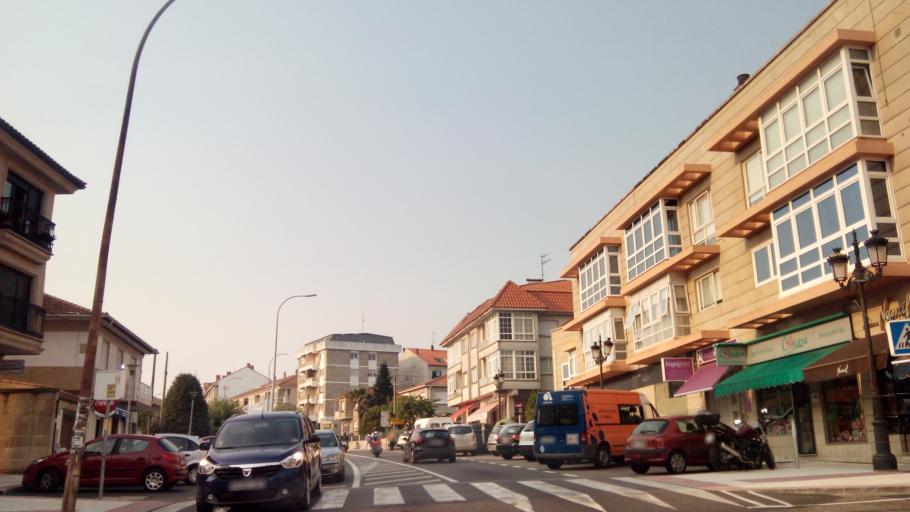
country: ES
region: Galicia
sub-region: Provincia de Pontevedra
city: Nigran
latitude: 42.1405
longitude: -8.8064
